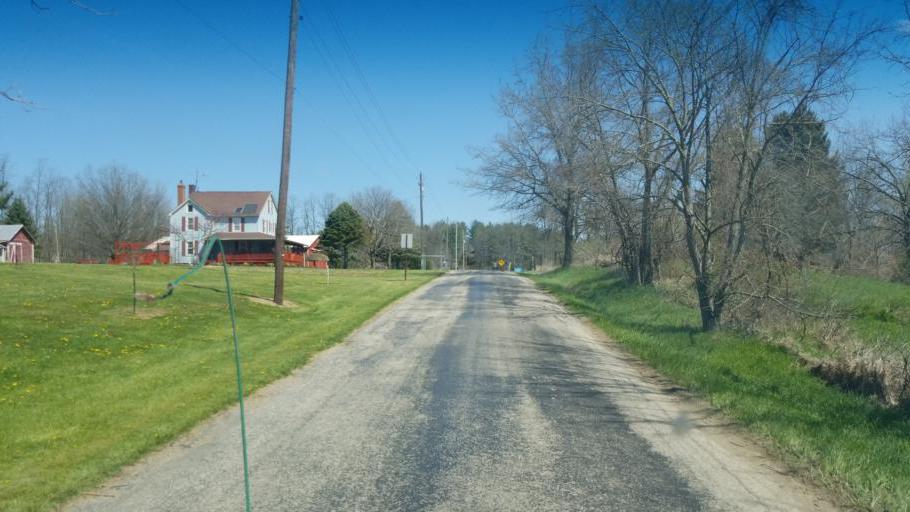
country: US
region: Ohio
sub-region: Richland County
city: Lincoln Heights
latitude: 40.8166
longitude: -82.4262
